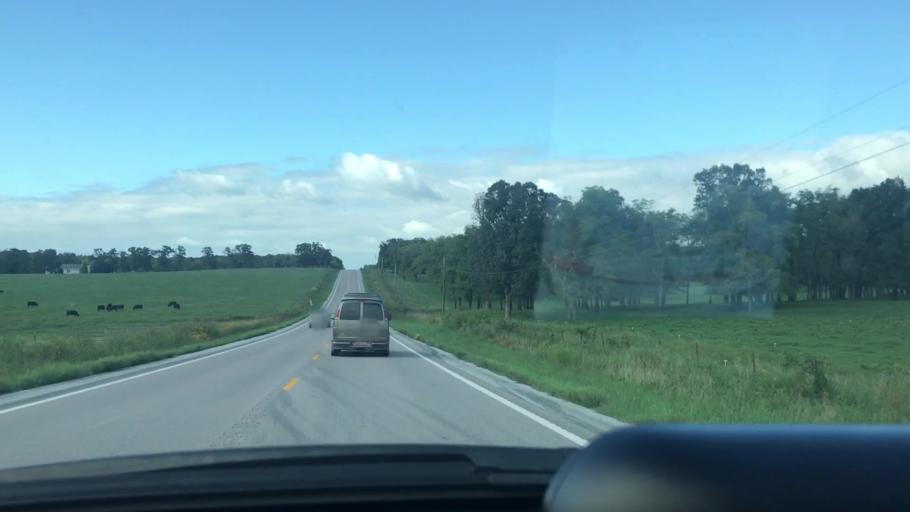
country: US
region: Missouri
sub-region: Hickory County
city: Hermitage
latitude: 37.9693
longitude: -93.2064
